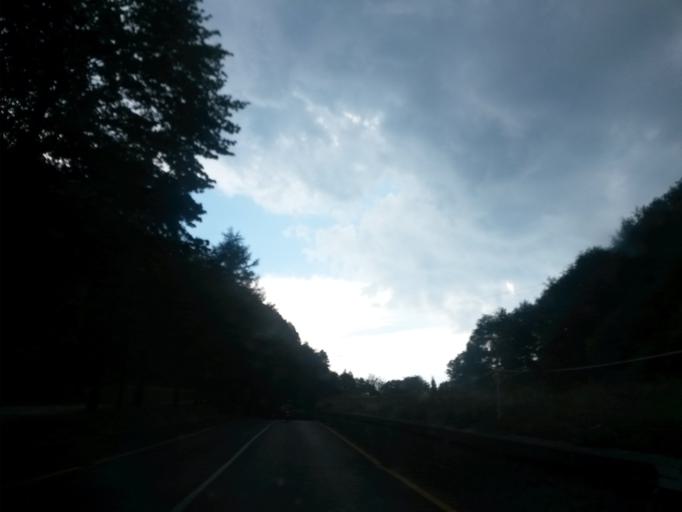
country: IT
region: Lombardy
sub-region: Provincia di Brescia
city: Gardola
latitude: 45.7448
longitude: 10.7322
